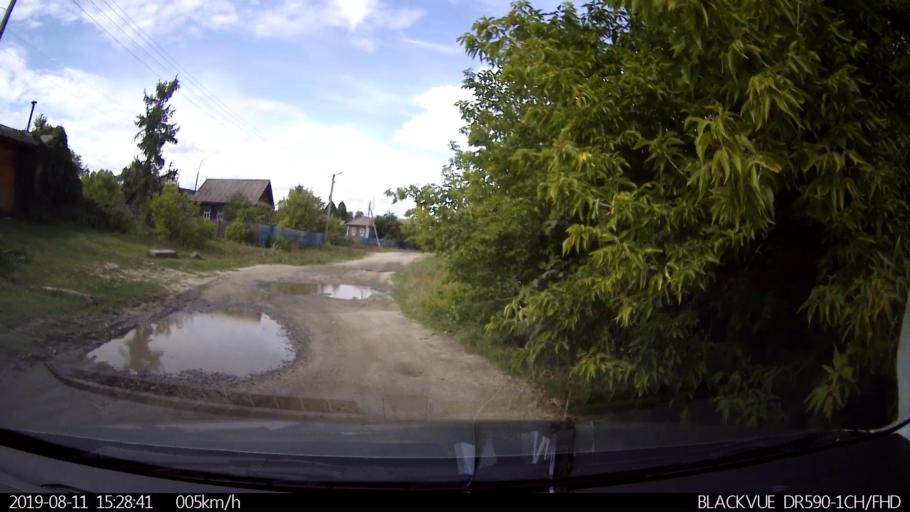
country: RU
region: Ulyanovsk
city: Ignatovka
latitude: 53.8530
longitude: 47.5745
